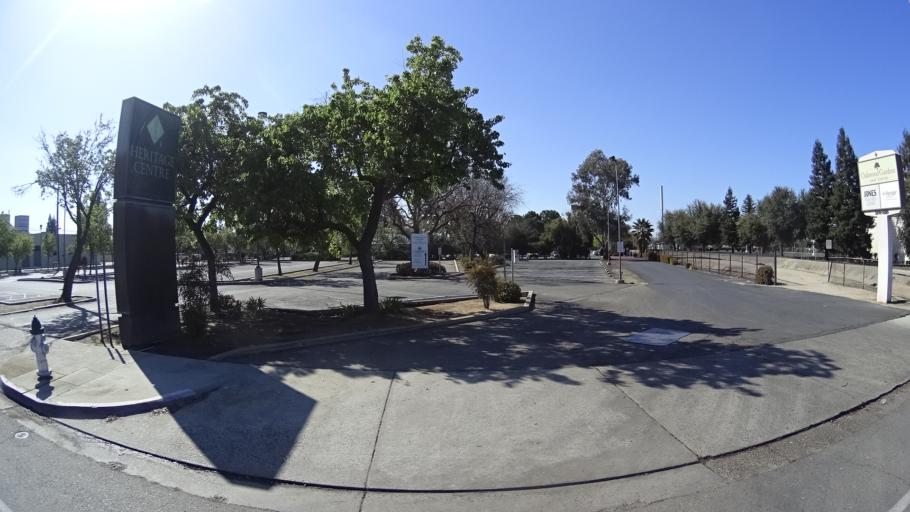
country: US
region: California
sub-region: Fresno County
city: Fresno
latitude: 36.7795
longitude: -119.7661
